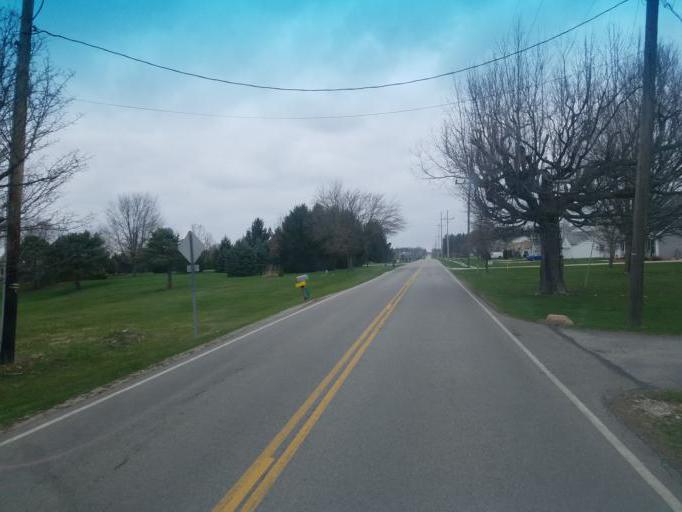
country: US
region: Ohio
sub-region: Marion County
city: Marion
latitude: 40.5212
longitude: -83.1509
